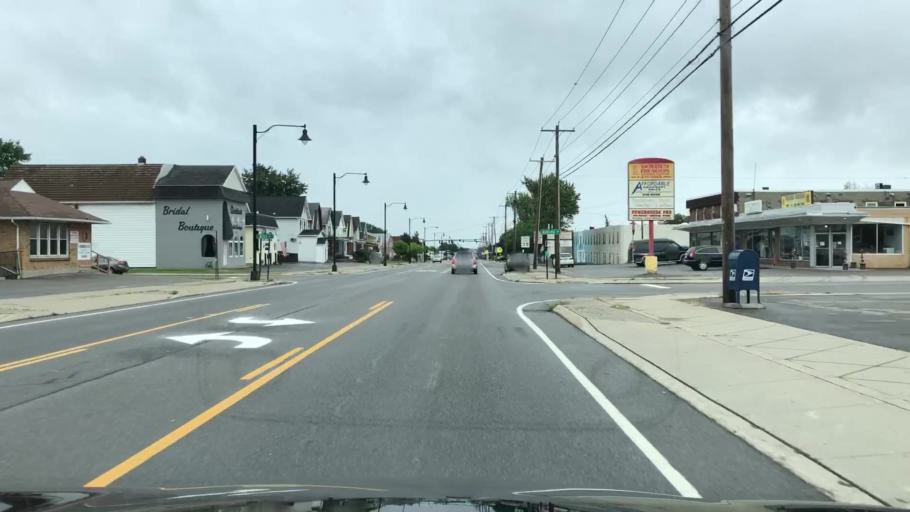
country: US
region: New York
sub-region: Erie County
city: Eggertsville
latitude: 42.9435
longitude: -78.7842
